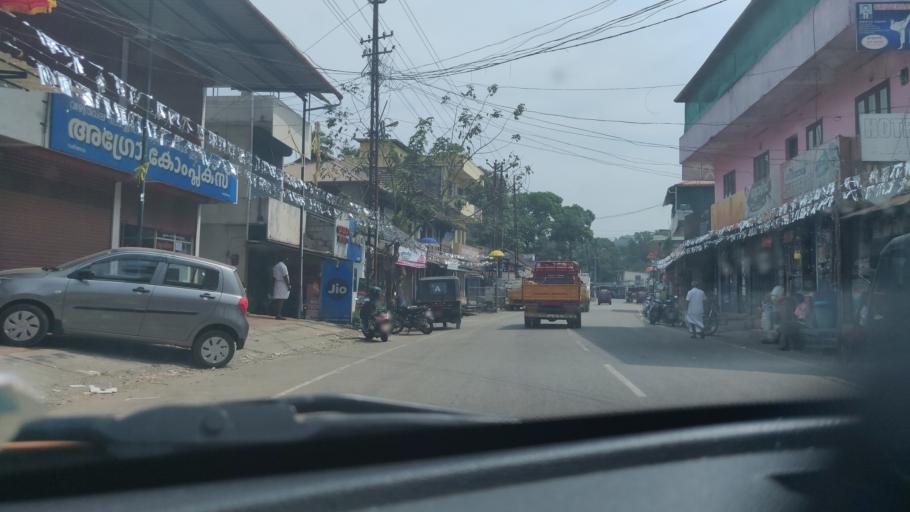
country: IN
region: Kerala
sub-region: Ernakulam
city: Muvattupuzha
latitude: 9.8835
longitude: 76.6433
